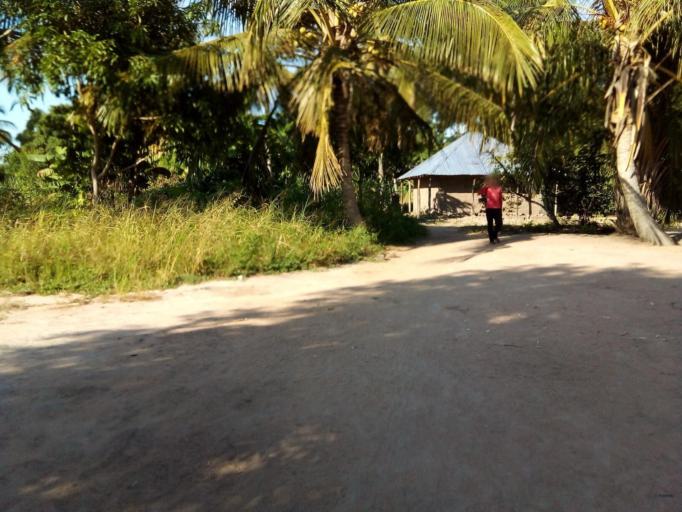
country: MZ
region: Zambezia
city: Quelimane
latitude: -17.5742
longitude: 36.8654
